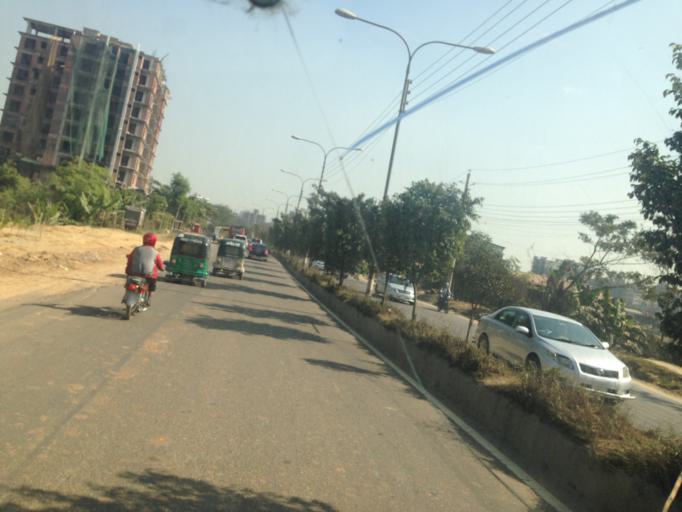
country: BD
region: Dhaka
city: Tungi
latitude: 23.8203
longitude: 90.3870
